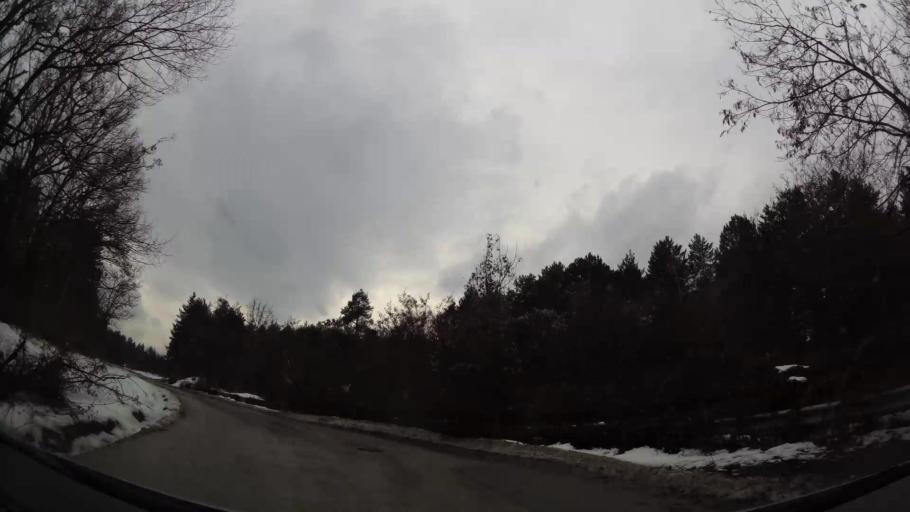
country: BG
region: Sofiya
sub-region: Obshtina Bozhurishte
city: Bozhurishte
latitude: 42.6743
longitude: 23.2213
